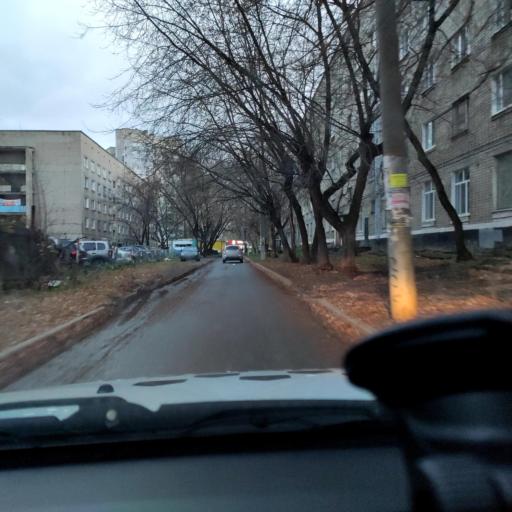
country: RU
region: Perm
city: Perm
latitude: 57.9772
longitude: 56.2305
